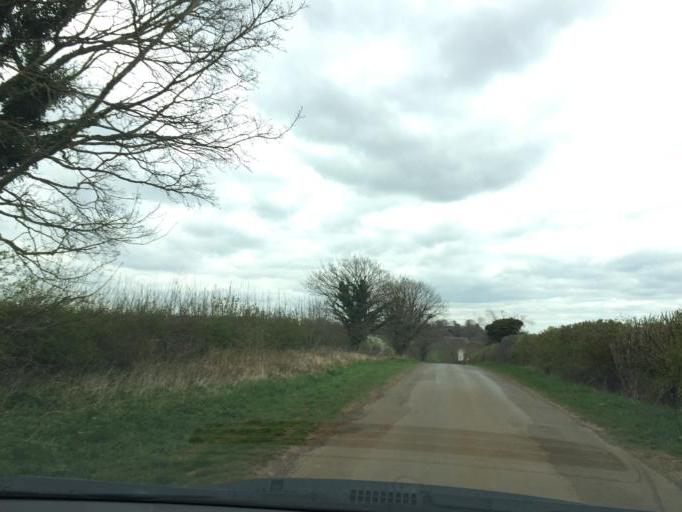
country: GB
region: England
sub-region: Oxfordshire
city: Hanwell
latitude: 52.0849
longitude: -1.3923
